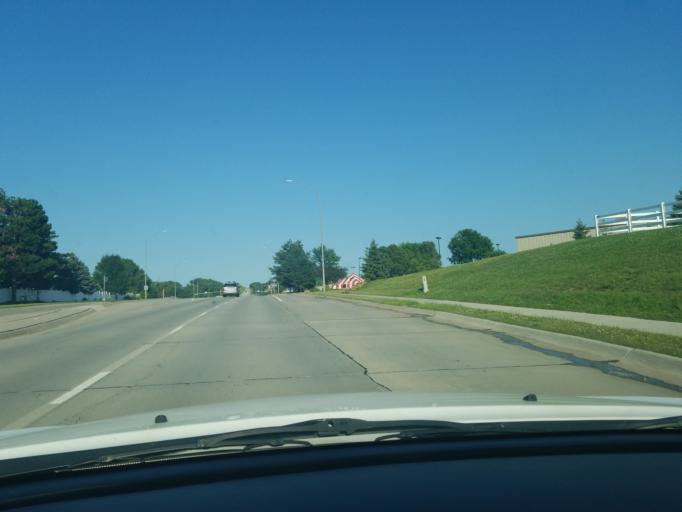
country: US
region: Nebraska
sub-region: Lancaster County
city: Lincoln
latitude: 40.7552
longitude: -96.6099
